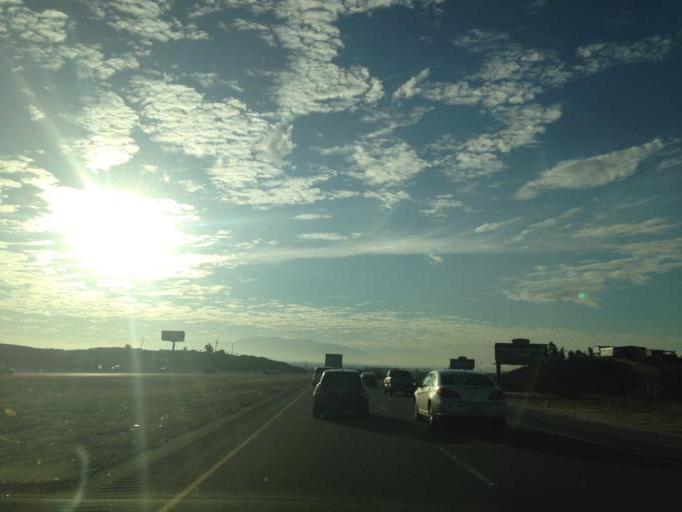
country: US
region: California
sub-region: Riverside County
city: Murrieta Hot Springs
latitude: 33.5440
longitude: -117.1786
